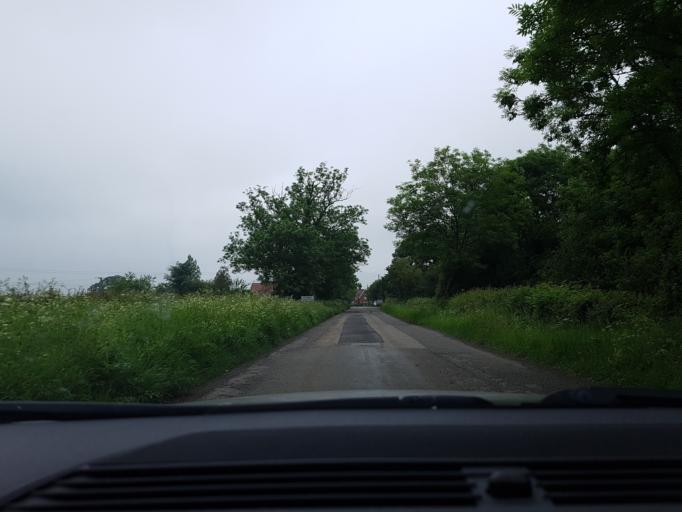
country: GB
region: England
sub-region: Buckinghamshire
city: Winslow
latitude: 51.9393
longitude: -0.9263
